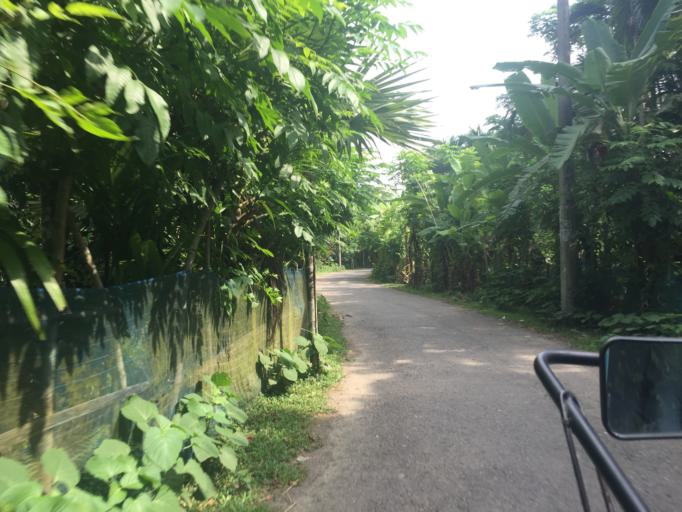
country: BD
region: Barisal
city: Mathba
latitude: 22.2411
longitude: 89.9146
